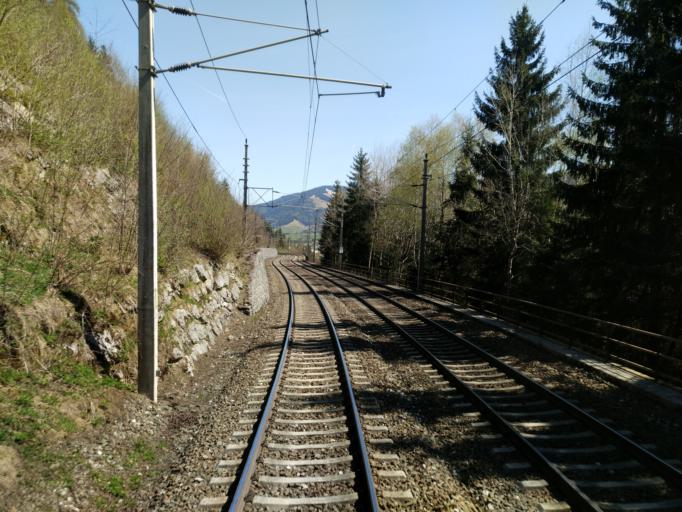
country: AT
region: Salzburg
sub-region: Politischer Bezirk Zell am See
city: Leogang
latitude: 47.4434
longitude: 12.7085
